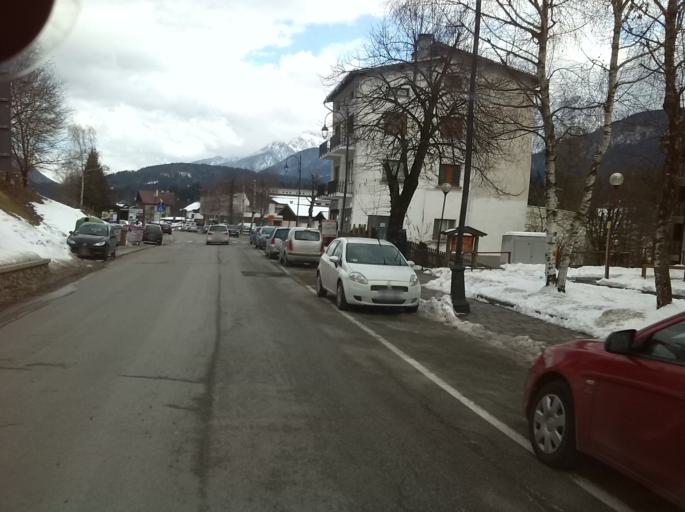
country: IT
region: Friuli Venezia Giulia
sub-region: Provincia di Udine
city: Tarvisio
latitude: 46.5049
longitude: 13.5740
